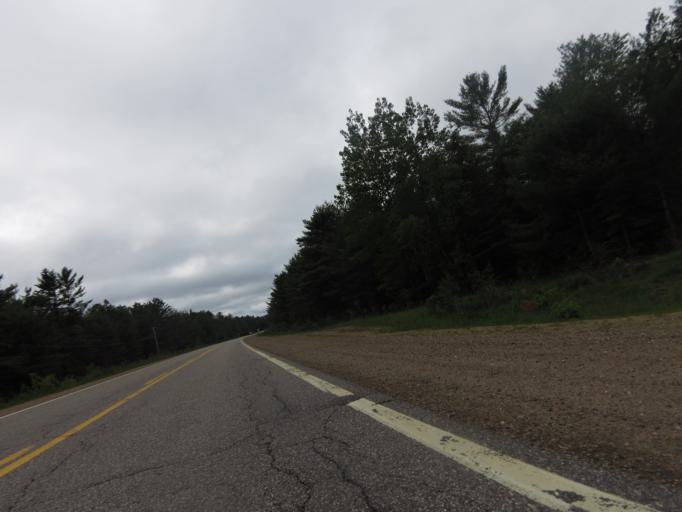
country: CA
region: Quebec
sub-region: Outaouais
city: Shawville
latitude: 45.8636
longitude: -76.4078
